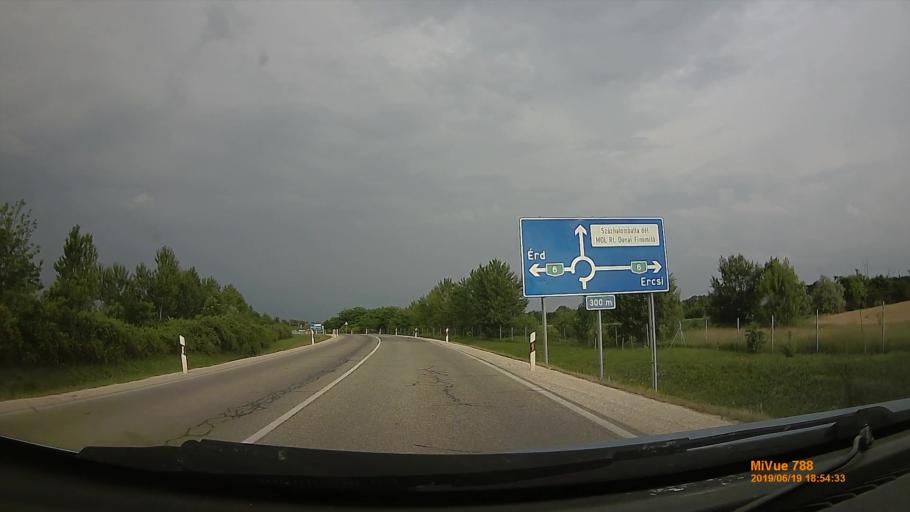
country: HU
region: Pest
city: Szazhalombatta
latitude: 47.3014
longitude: 18.8800
